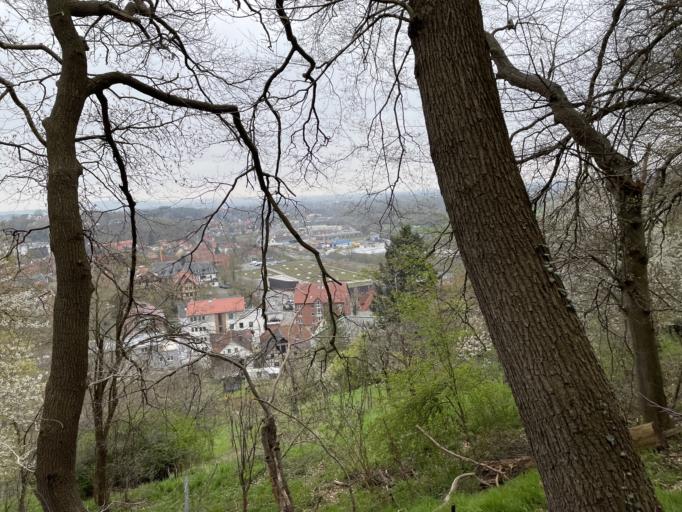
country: DE
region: North Rhine-Westphalia
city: Porta Westfalica
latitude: 52.2414
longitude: 8.9239
